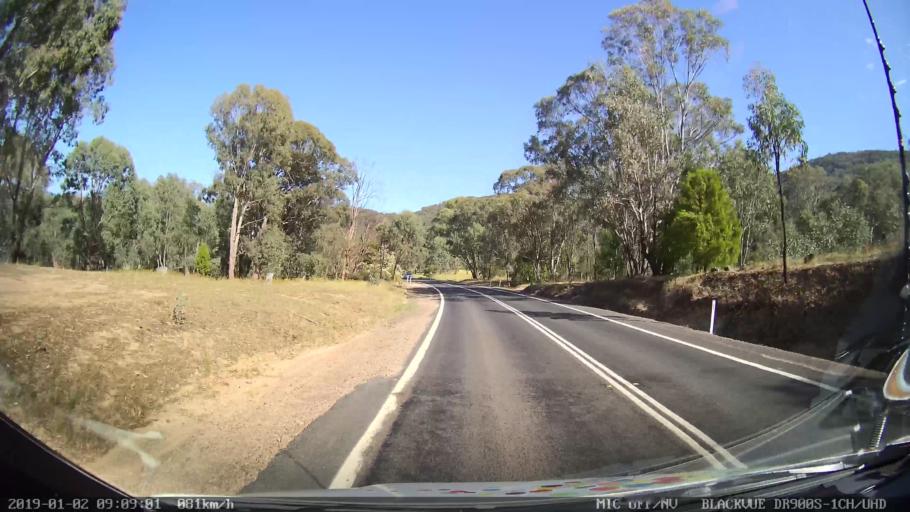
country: AU
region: New South Wales
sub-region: Tumut Shire
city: Tumut
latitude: -35.5267
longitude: 148.2855
